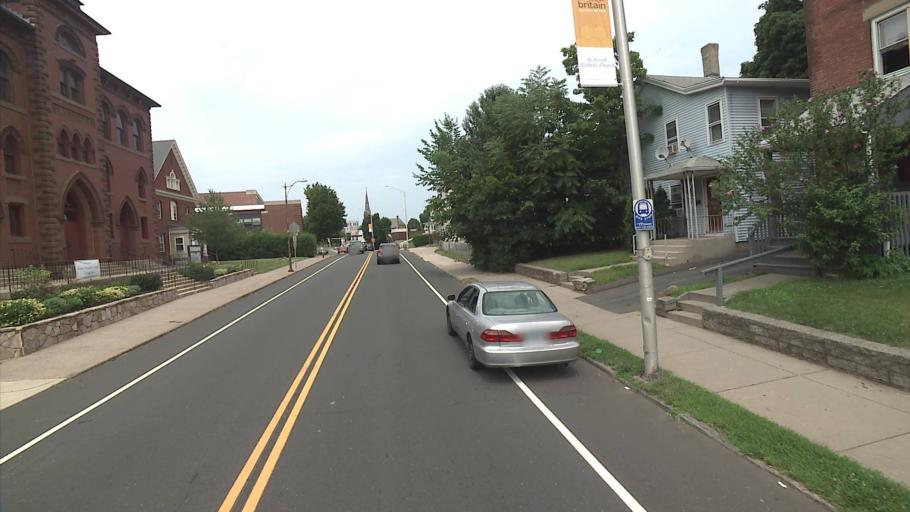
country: US
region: Connecticut
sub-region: Hartford County
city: New Britain
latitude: 41.6588
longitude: -72.7779
